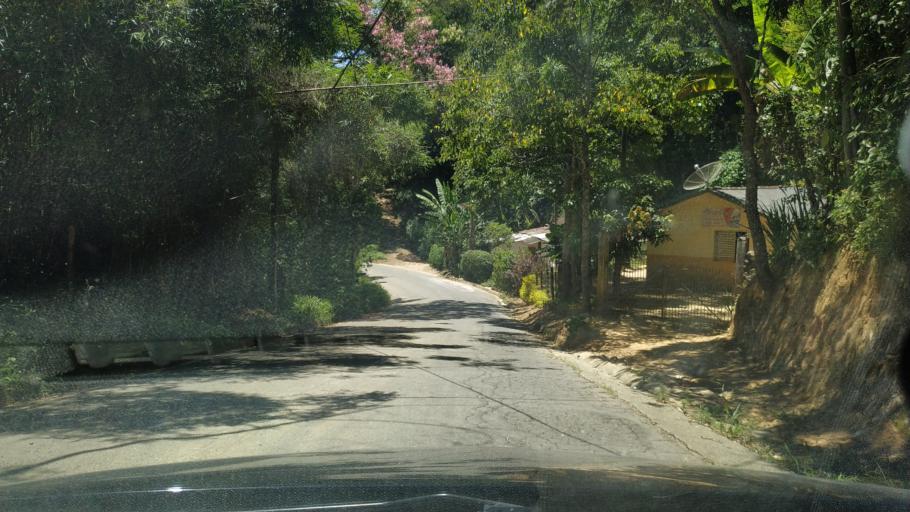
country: BR
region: Sao Paulo
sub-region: Campos Do Jordao
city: Campos do Jordao
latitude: -22.8087
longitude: -45.6894
